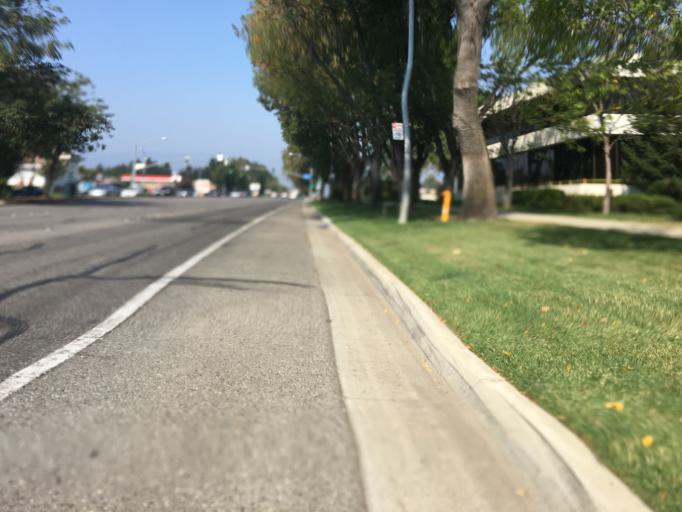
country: US
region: California
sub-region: Santa Clara County
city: Cupertino
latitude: 37.3231
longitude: -122.0127
